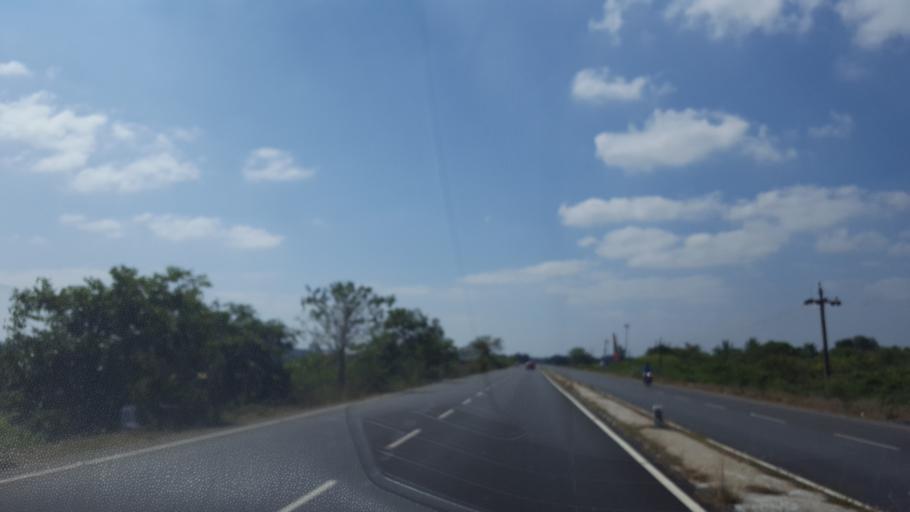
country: IN
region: Tamil Nadu
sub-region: Kancheepuram
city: Mamallapuram
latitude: 12.6654
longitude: 80.1778
